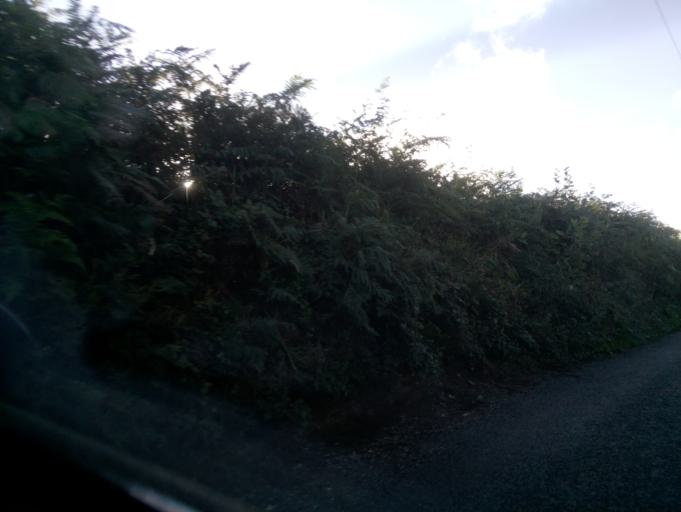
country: GB
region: England
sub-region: Devon
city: Dartmouth
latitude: 50.3419
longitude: -3.6088
